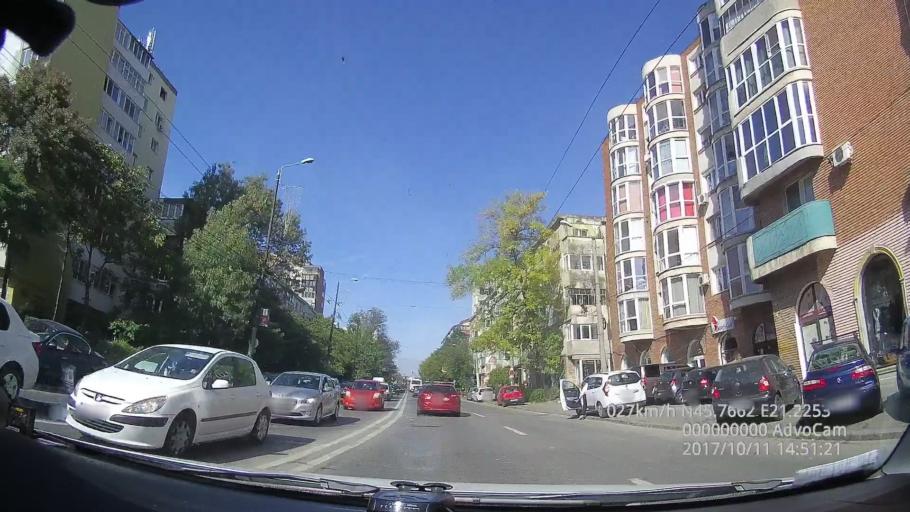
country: RO
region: Timis
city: Timisoara
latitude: 45.7663
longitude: 21.2252
